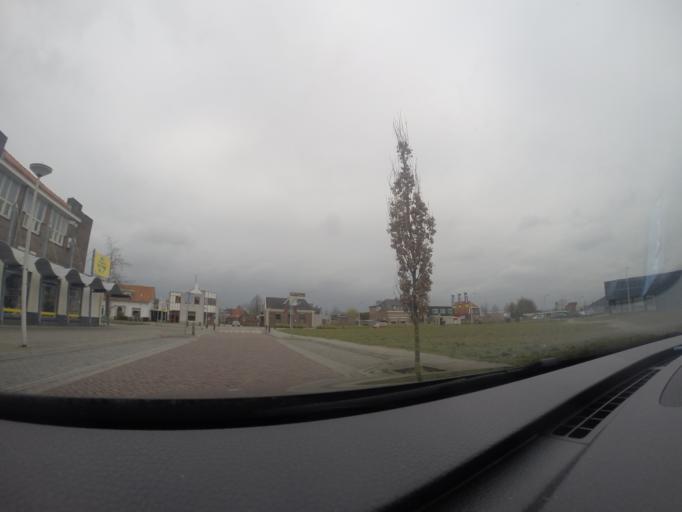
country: NL
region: Gelderland
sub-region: Berkelland
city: Borculo
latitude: 52.1186
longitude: 6.5232
